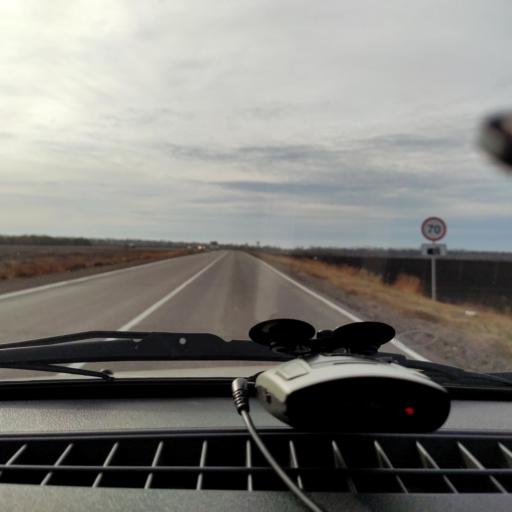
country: RU
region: Voronezj
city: Strelitsa
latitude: 51.4706
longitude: 38.9595
